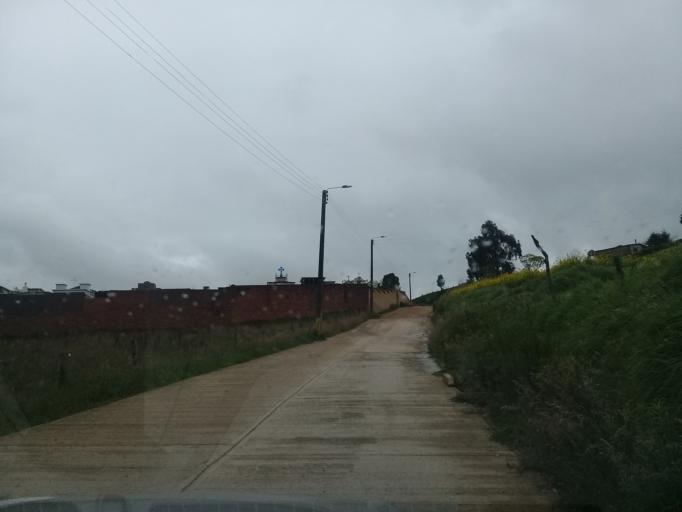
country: CO
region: Boyaca
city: Samaca
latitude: 5.4468
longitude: -73.4355
